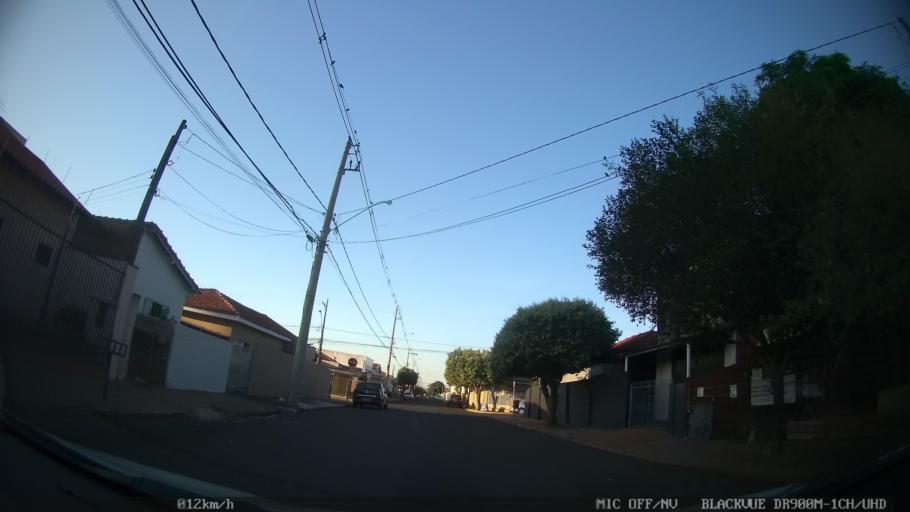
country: BR
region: Sao Paulo
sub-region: Sao Jose Do Rio Preto
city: Sao Jose do Rio Preto
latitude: -20.7968
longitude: -49.3897
